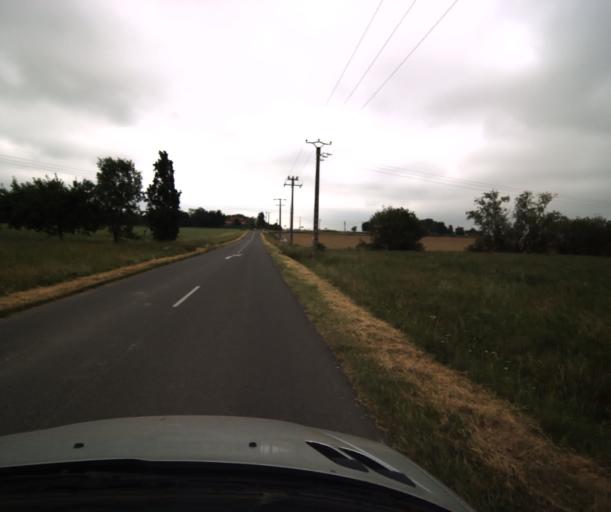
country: FR
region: Midi-Pyrenees
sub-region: Departement du Tarn-et-Garonne
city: Saint-Nicolas-de-la-Grave
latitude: 44.0378
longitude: 1.0105
